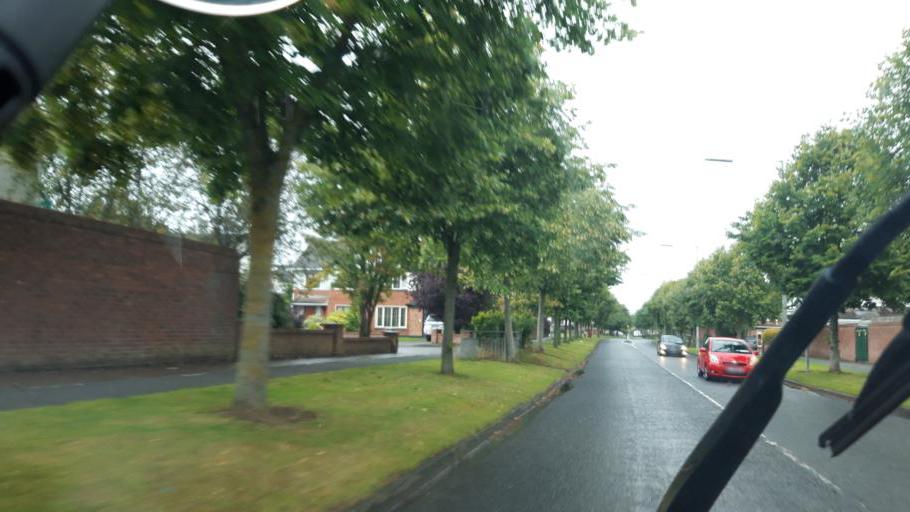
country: IE
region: Leinster
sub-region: Fingal County
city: Blanchardstown
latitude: 53.3714
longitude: -6.3961
